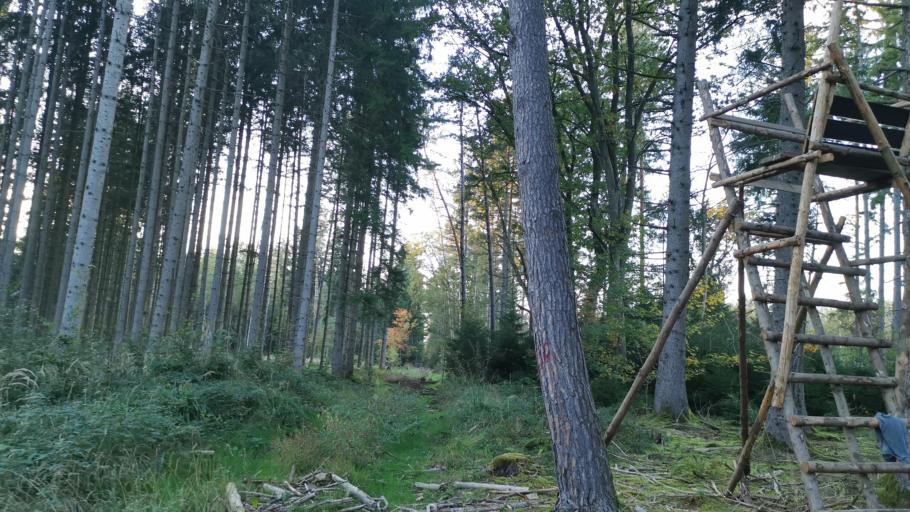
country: DE
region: Bavaria
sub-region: Upper Bavaria
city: Neuried
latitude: 48.0712
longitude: 11.4642
